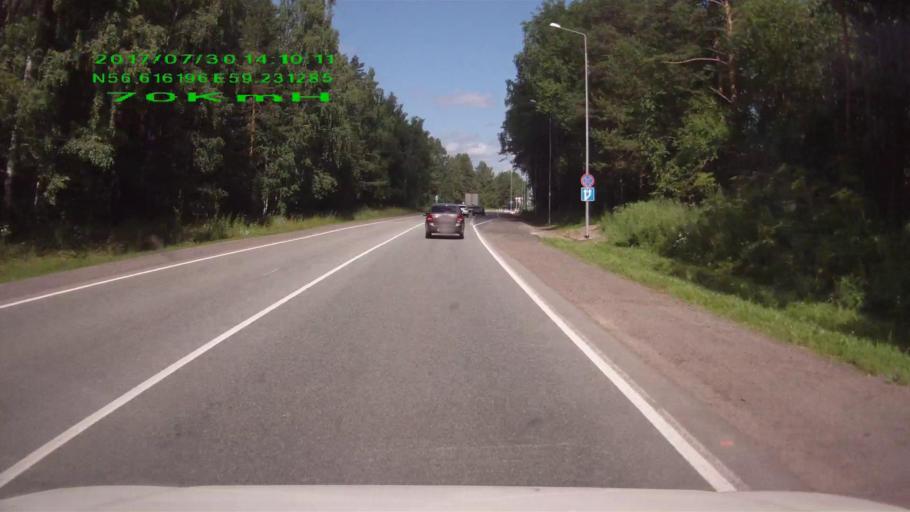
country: RU
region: Sverdlovsk
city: Nizhniye Sergi
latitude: 56.6165
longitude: 59.2315
